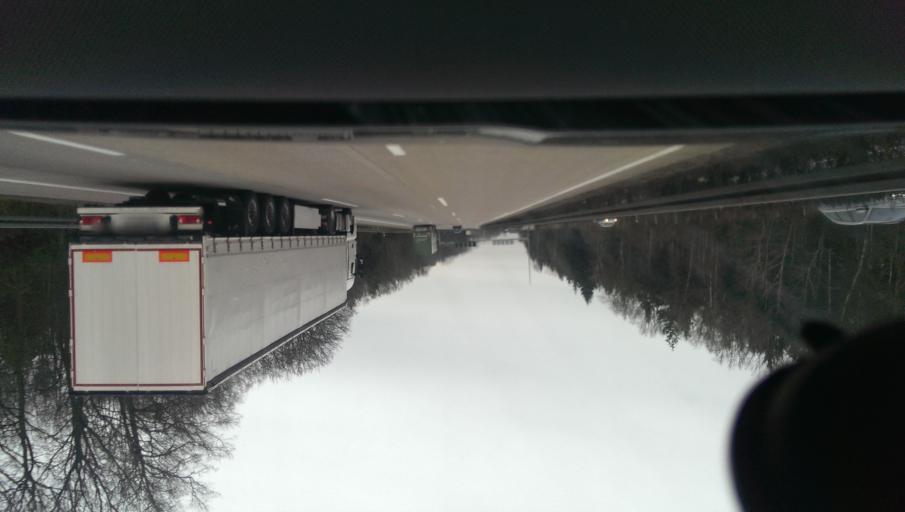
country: DE
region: Lower Saxony
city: Isernhagen Farster Bauerschaft
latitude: 52.4590
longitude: 9.8597
